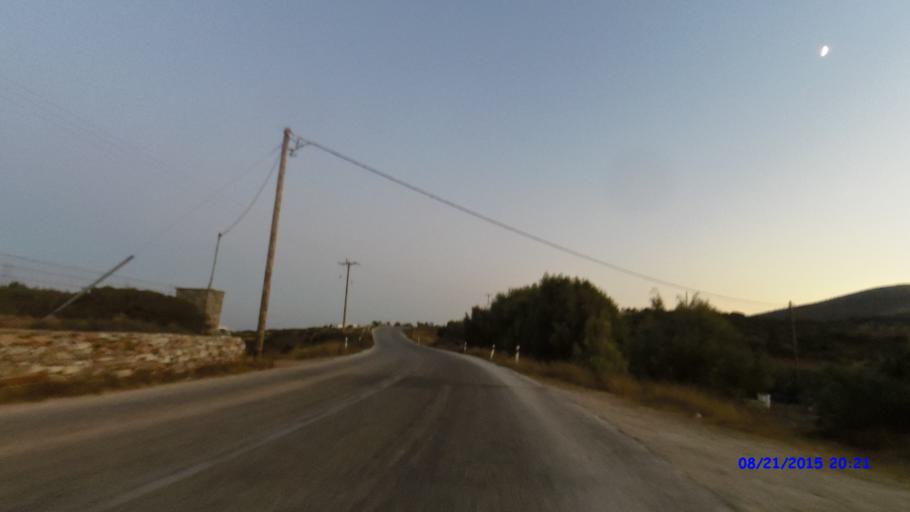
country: GR
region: South Aegean
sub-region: Nomos Kykladon
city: Antiparos
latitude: 36.9985
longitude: 25.0715
